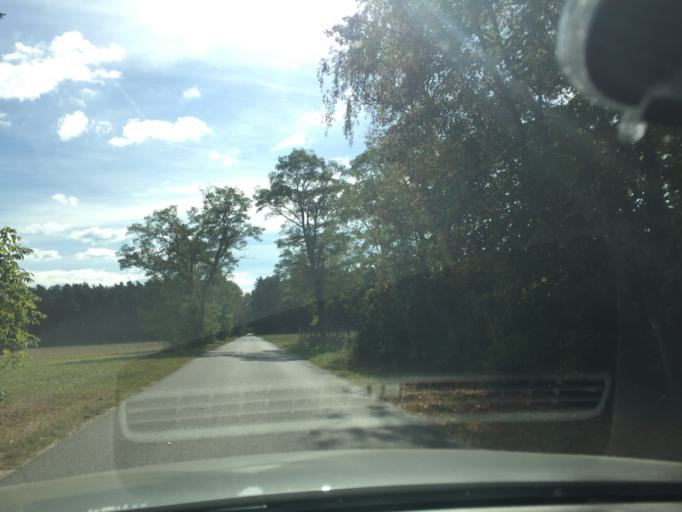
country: DE
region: Brandenburg
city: Spreenhagen
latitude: 52.3619
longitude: 13.8779
